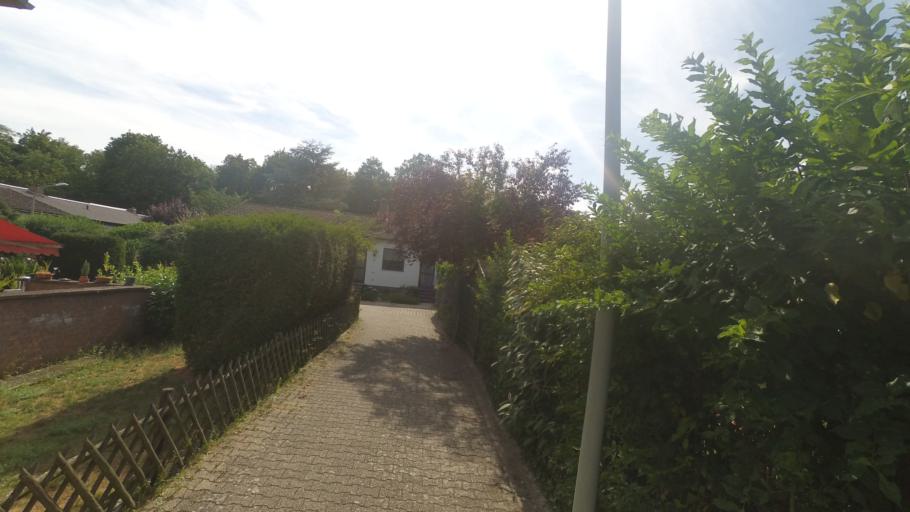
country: DE
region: Rheinland-Pfalz
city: Limburgerhof
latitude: 49.4166
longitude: 8.3826
